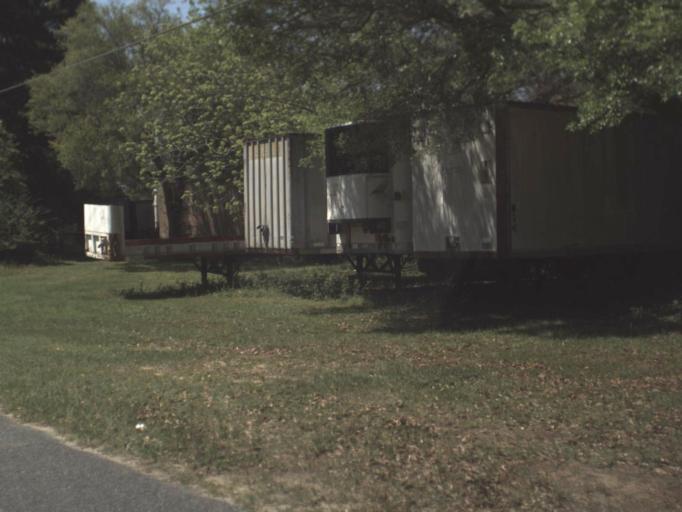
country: US
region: Florida
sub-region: Escambia County
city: Cantonment
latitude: 30.5346
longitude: -87.4043
